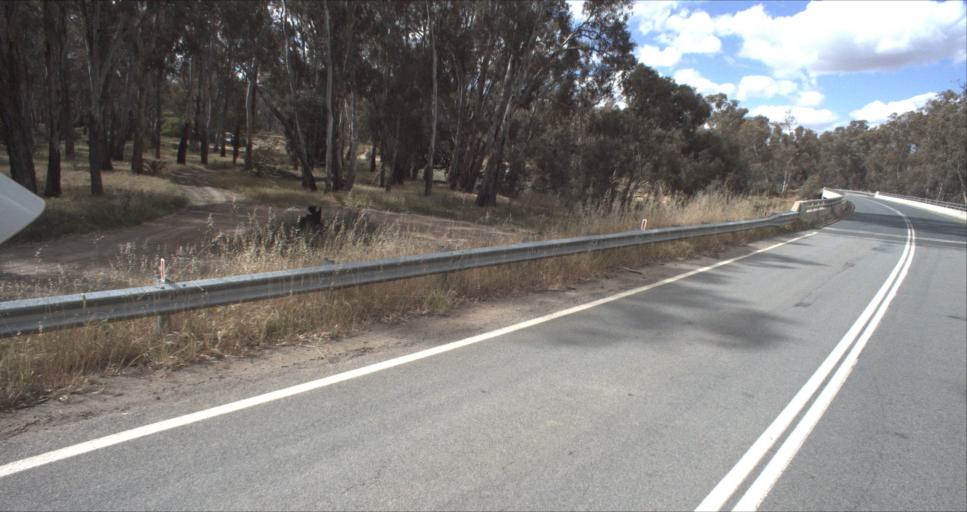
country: AU
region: New South Wales
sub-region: Leeton
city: Leeton
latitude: -34.6392
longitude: 146.3731
